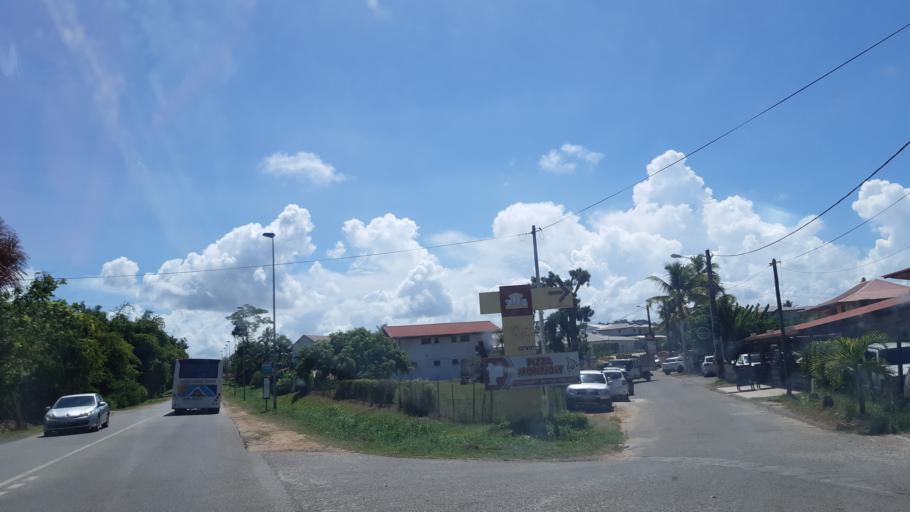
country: GF
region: Guyane
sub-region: Guyane
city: Remire-Montjoly
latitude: 4.9183
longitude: -52.2794
